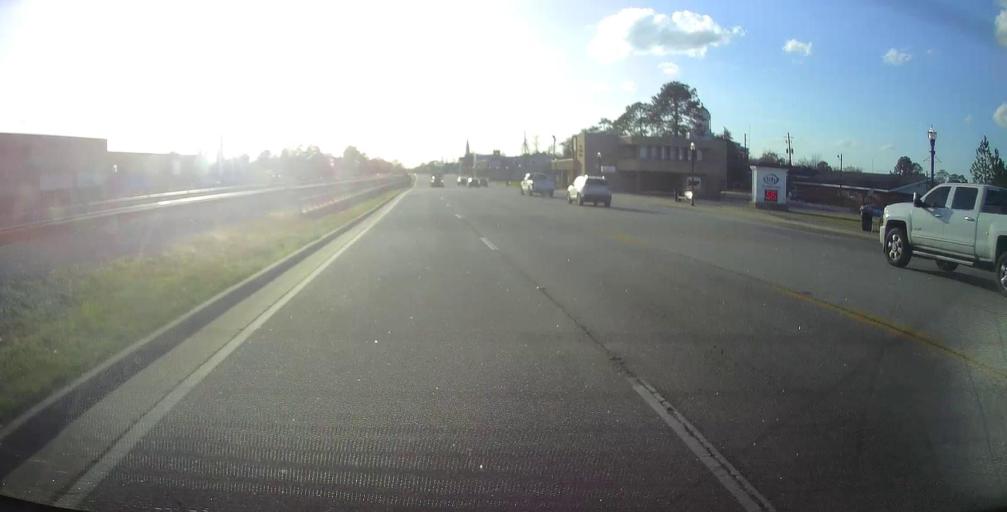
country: US
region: Georgia
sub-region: Evans County
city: Claxton
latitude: 32.1612
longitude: -81.9059
